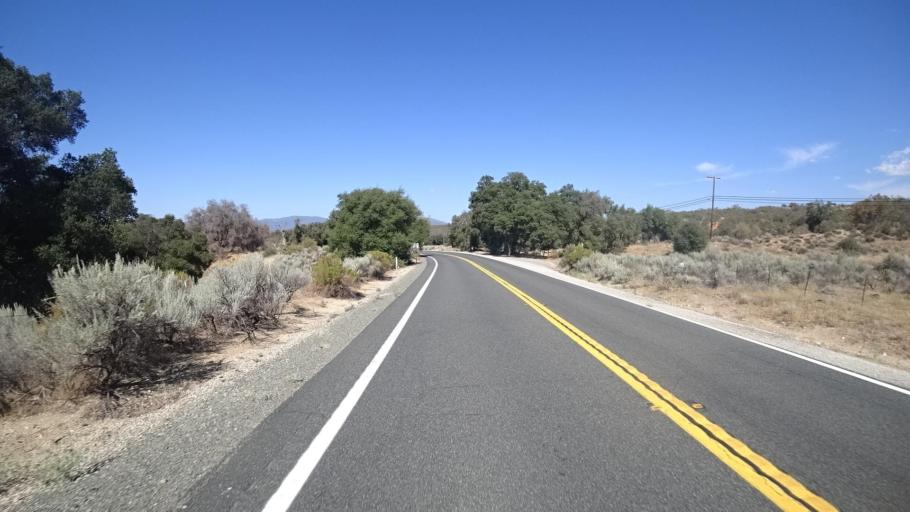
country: US
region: California
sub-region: San Diego County
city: Julian
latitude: 33.2871
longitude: -116.6451
